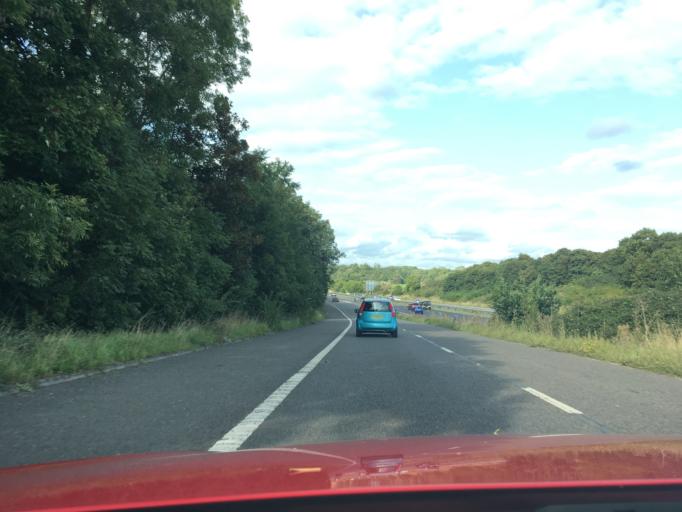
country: GB
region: England
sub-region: South Gloucestershire
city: Falfield
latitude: 51.6376
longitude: -2.4518
